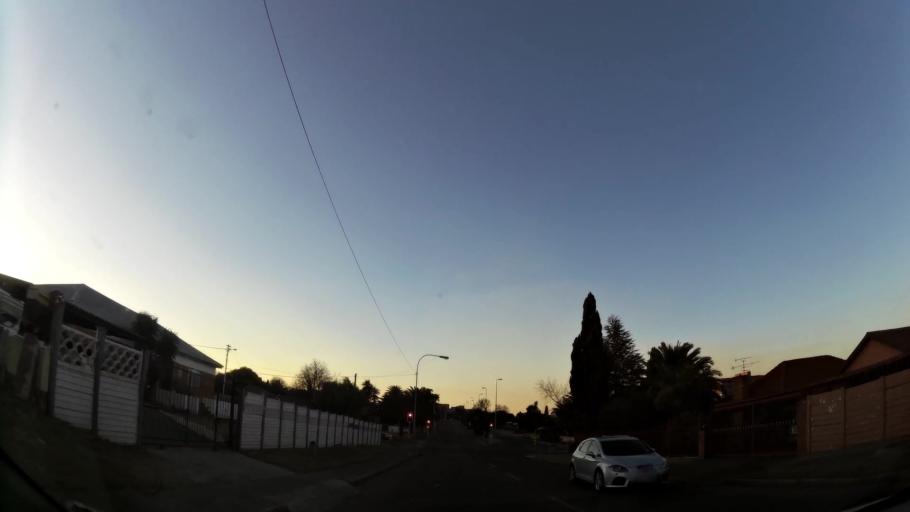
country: ZA
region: Gauteng
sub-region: City of Johannesburg Metropolitan Municipality
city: Roodepoort
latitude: -26.1599
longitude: 27.9000
